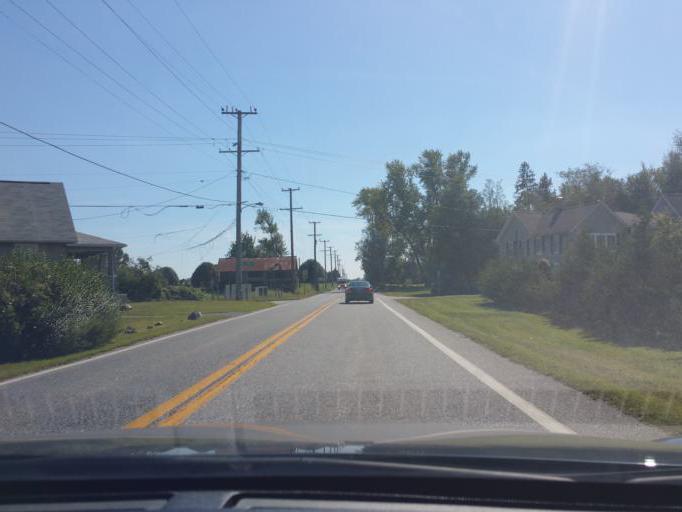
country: US
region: Maryland
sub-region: Harford County
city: Aberdeen
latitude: 39.5825
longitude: -76.1847
